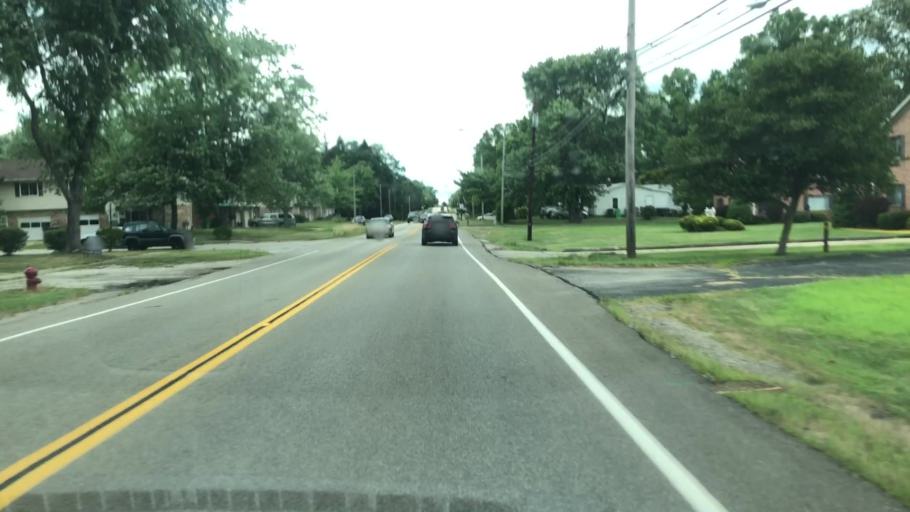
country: US
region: Ohio
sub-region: Summit County
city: Stow
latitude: 41.1796
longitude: -81.4179
